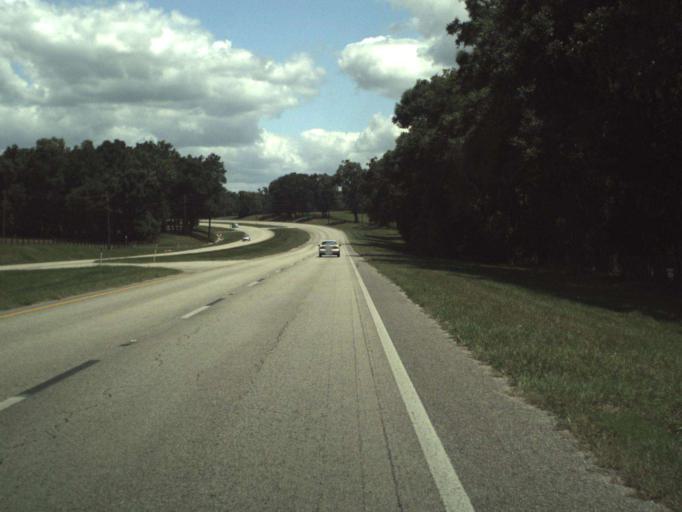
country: US
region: Florida
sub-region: Marion County
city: Citra
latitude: 29.3505
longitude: -82.1597
